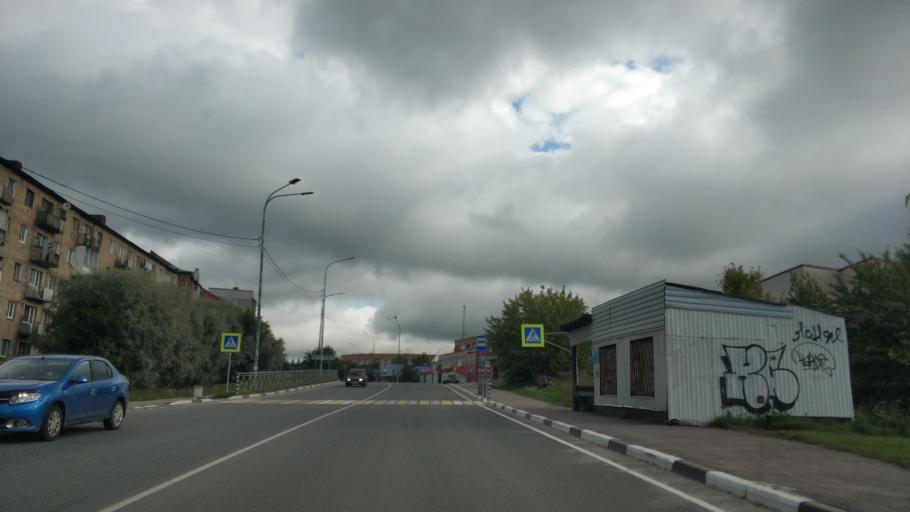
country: RU
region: Republic of Karelia
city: Sortavala
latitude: 61.7076
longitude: 30.6984
